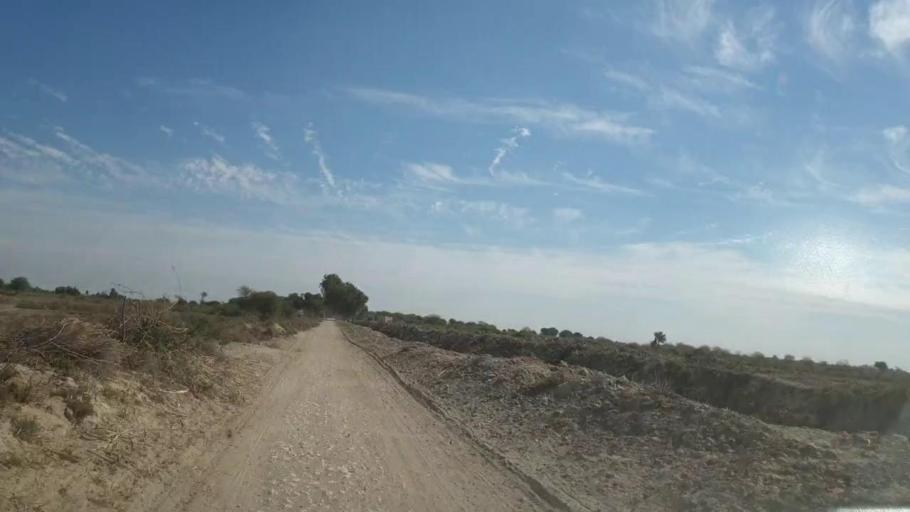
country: PK
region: Sindh
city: Pithoro
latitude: 25.5405
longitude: 69.3015
